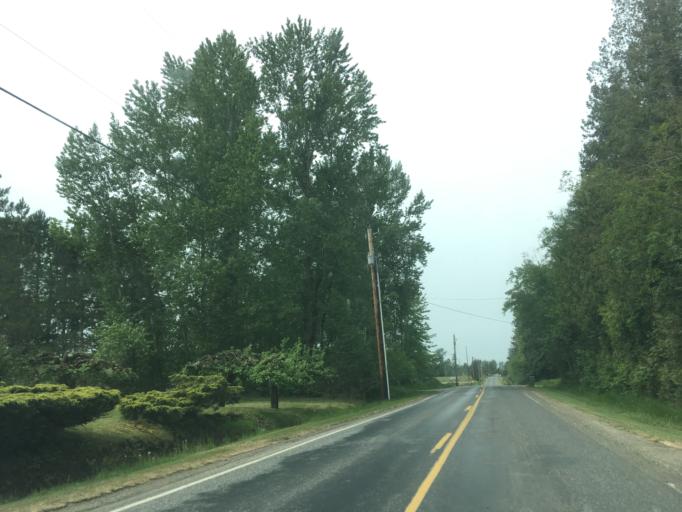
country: US
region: Washington
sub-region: Whatcom County
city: Bellingham
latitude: 48.8187
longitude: -122.4369
